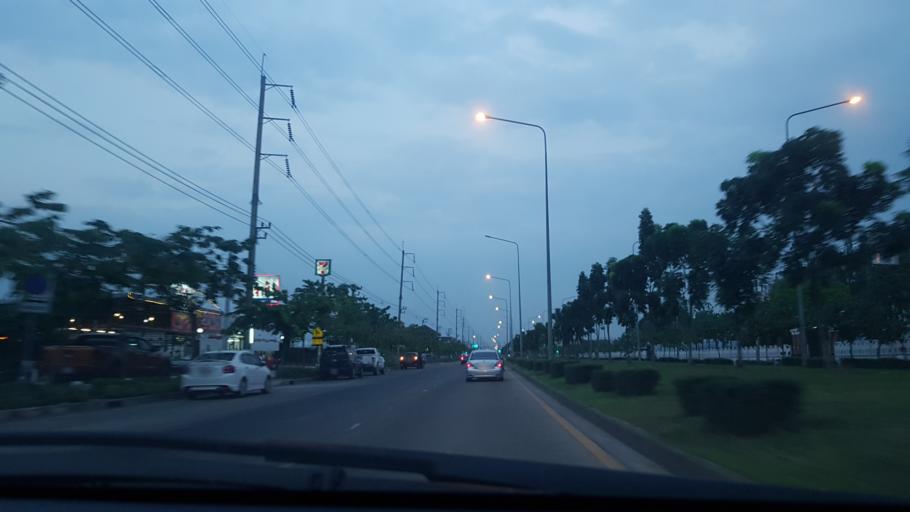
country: TH
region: Bangkok
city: Nong Khaem
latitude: 13.7322
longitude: 100.3638
